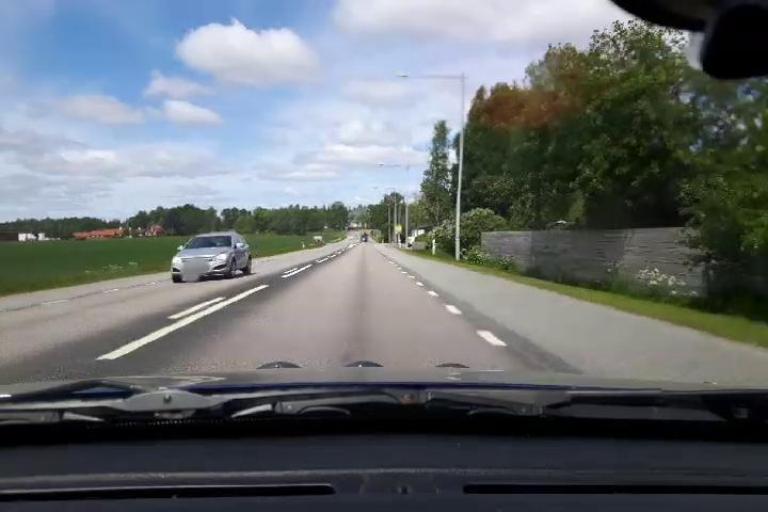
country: SE
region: Uppsala
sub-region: Osthammars Kommun
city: Bjorklinge
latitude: 60.0219
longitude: 17.5548
